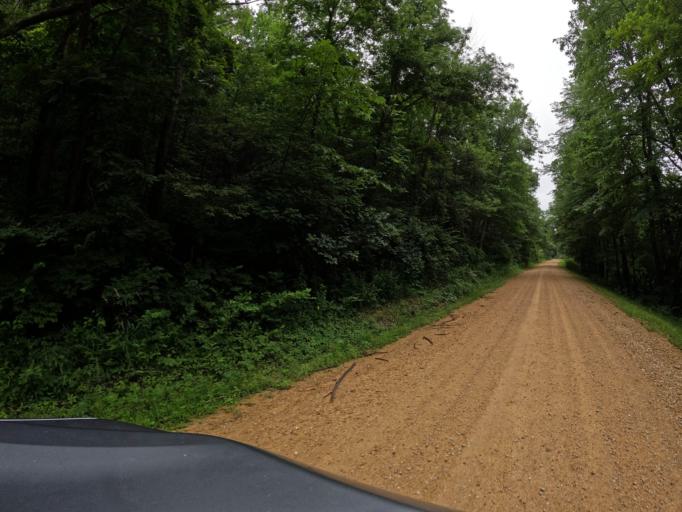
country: US
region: Illinois
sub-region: Carroll County
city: Savanna
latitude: 41.9866
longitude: -90.1729
